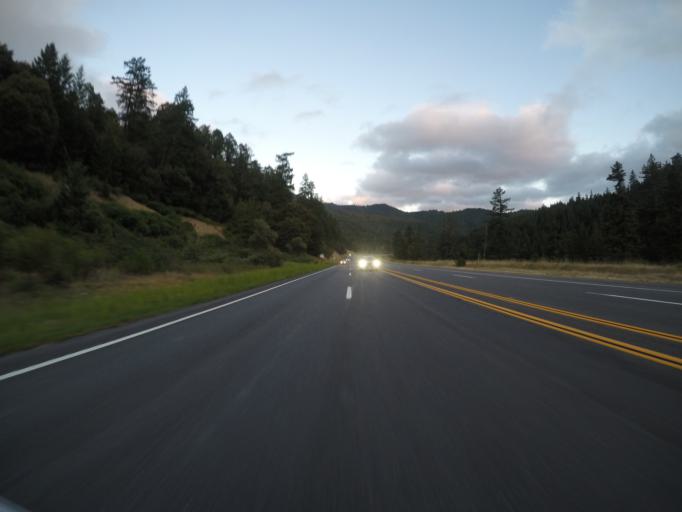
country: US
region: California
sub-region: Humboldt County
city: Redway
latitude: 40.0422
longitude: -123.7800
